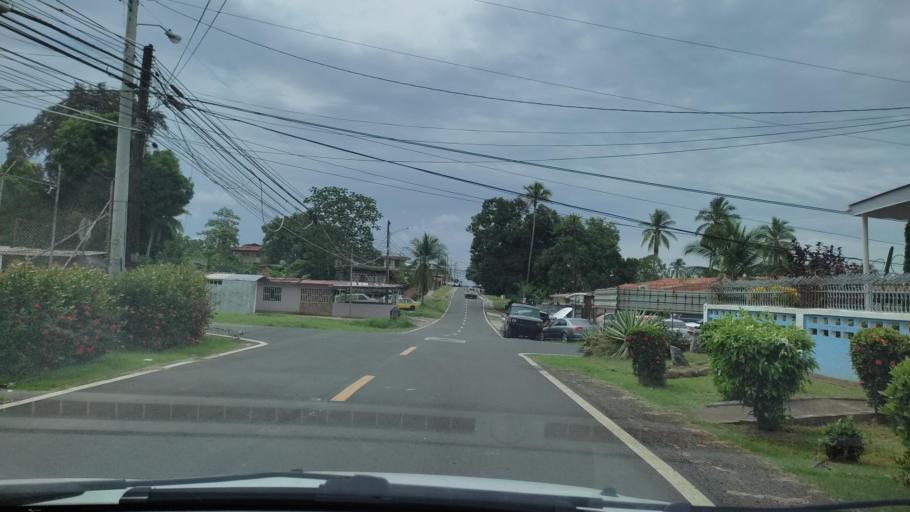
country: PA
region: Panama
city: San Miguelito
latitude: 9.0436
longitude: -79.4325
